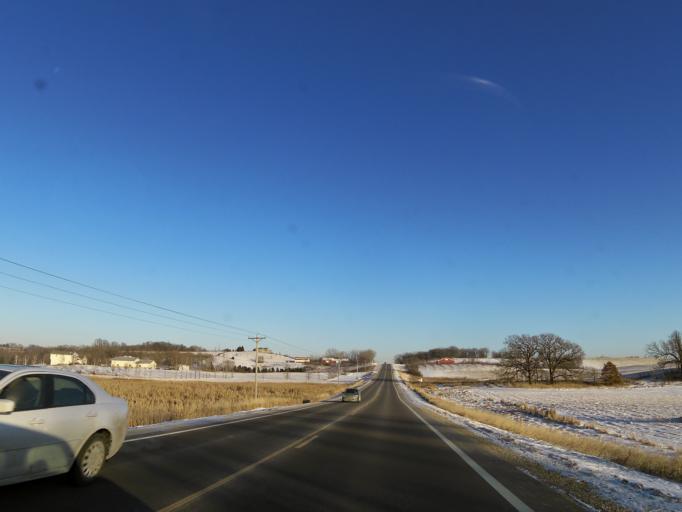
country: US
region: Minnesota
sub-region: Scott County
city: Elko New Market
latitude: 44.5439
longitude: -93.3649
